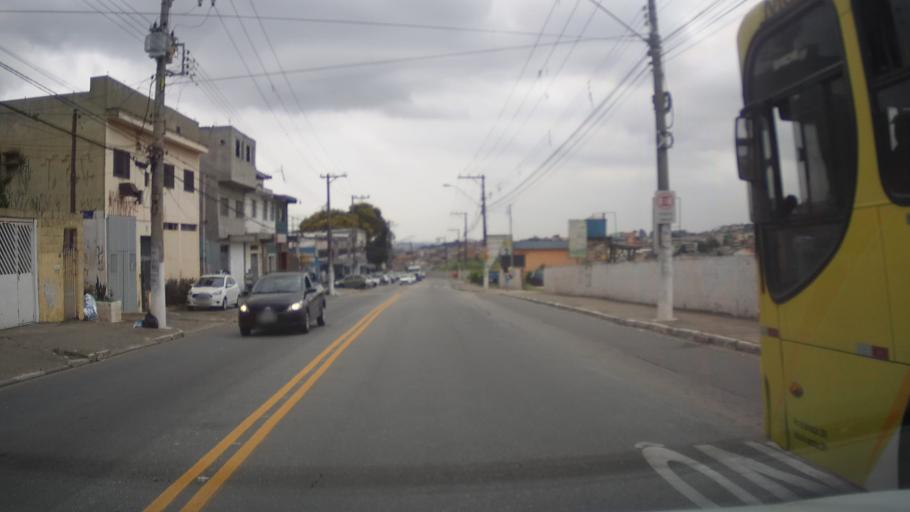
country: BR
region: Sao Paulo
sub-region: Itaquaquecetuba
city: Itaquaquecetuba
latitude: -23.4638
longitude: -46.4166
